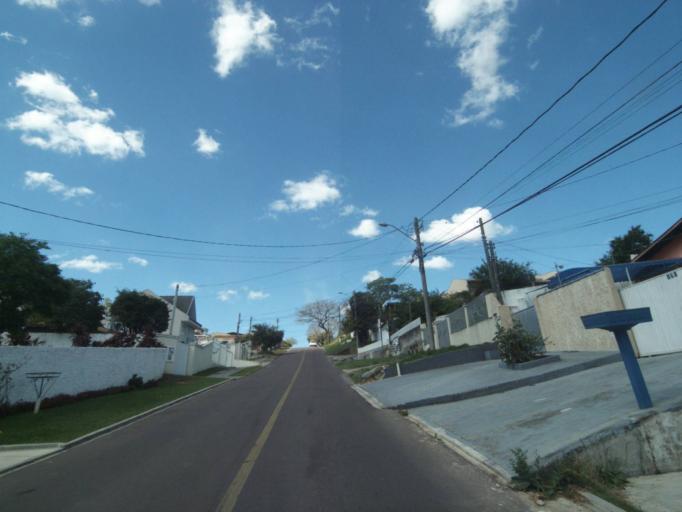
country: BR
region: Parana
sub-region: Curitiba
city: Curitiba
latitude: -25.3745
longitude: -49.2489
